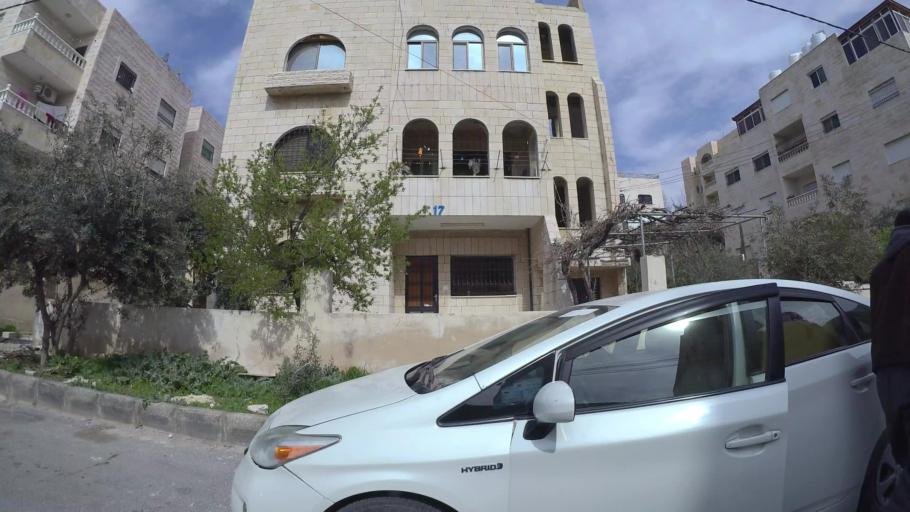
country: JO
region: Amman
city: Amman
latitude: 32.0007
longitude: 35.9373
